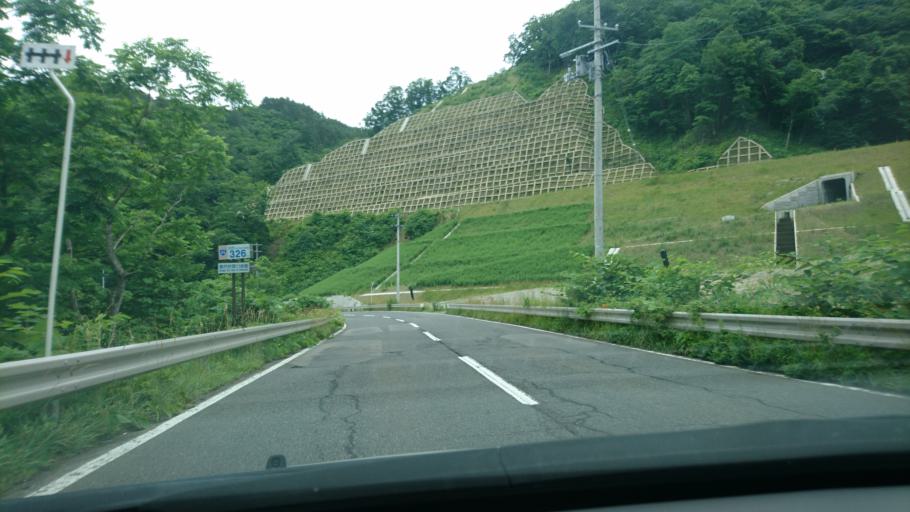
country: JP
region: Iwate
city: Miyako
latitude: 39.9885
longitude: 141.8681
